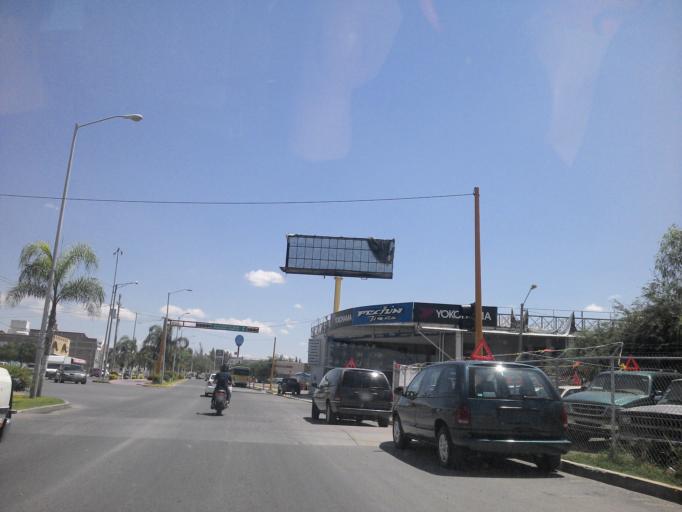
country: MX
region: Guanajuato
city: San Francisco del Rincon
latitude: 21.0276
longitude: -101.8727
